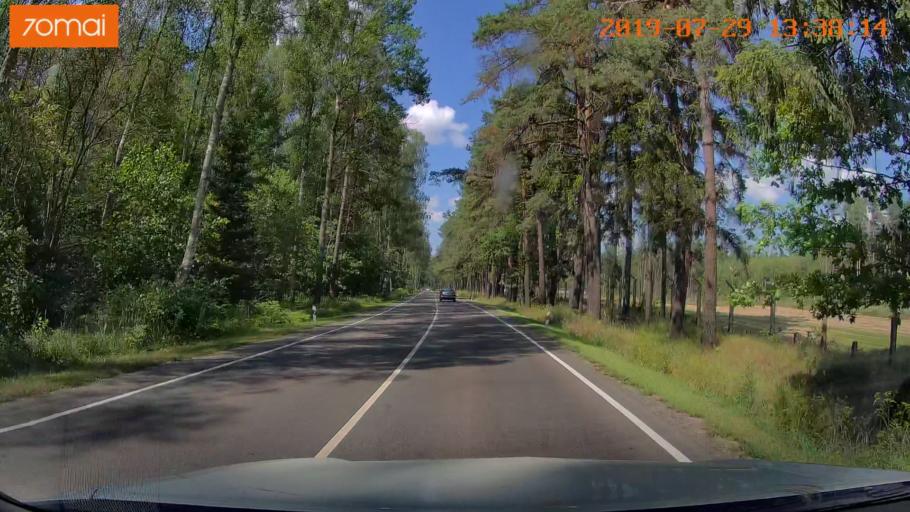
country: RU
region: Kaliningrad
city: Volochayevskoye
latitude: 54.7198
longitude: 20.1737
